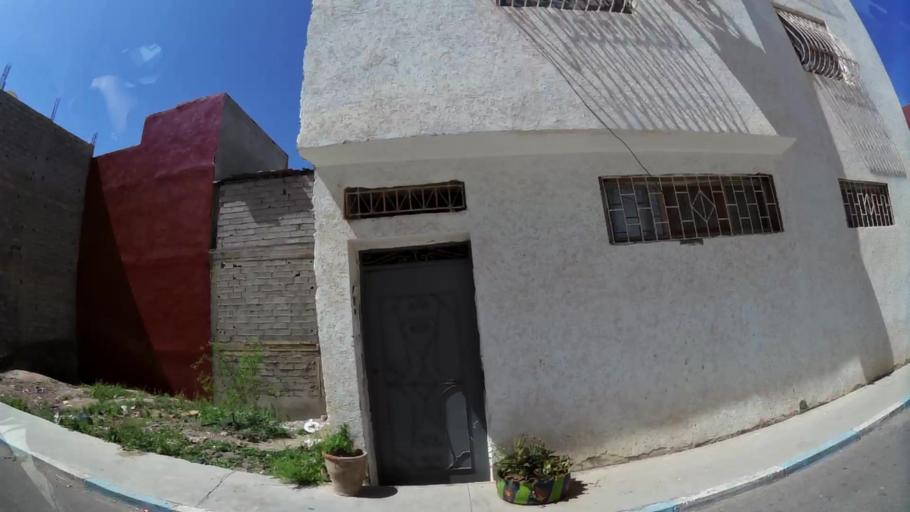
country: MA
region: Oued ed Dahab-Lagouira
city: Dakhla
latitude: 30.4410
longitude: -9.5545
